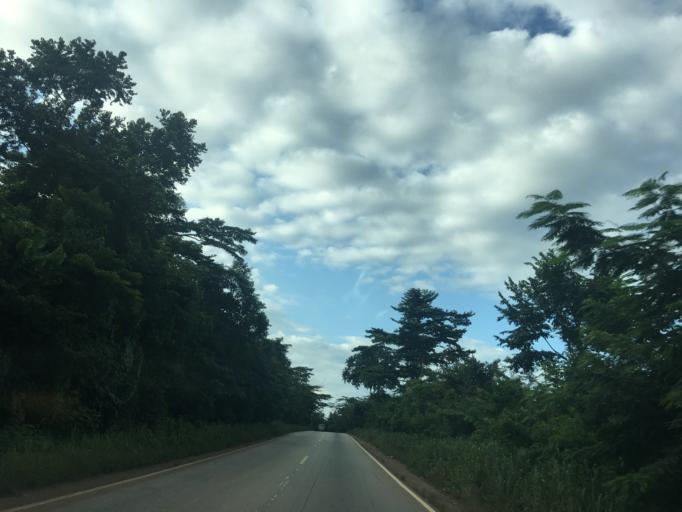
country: GH
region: Western
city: Bibiani
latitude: 6.4157
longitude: -2.3025
